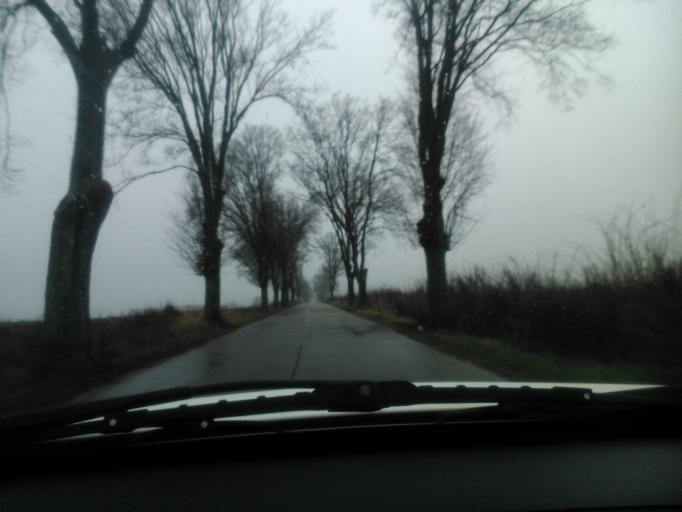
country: PL
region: Kujawsko-Pomorskie
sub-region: Powiat wabrzeski
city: Debowa Laka
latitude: 53.1977
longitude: 19.1616
